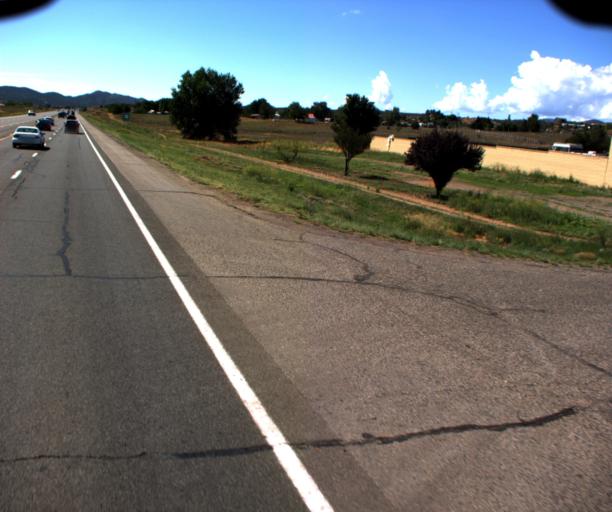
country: US
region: Arizona
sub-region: Yavapai County
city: Dewey-Humboldt
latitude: 34.5376
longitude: -112.2458
